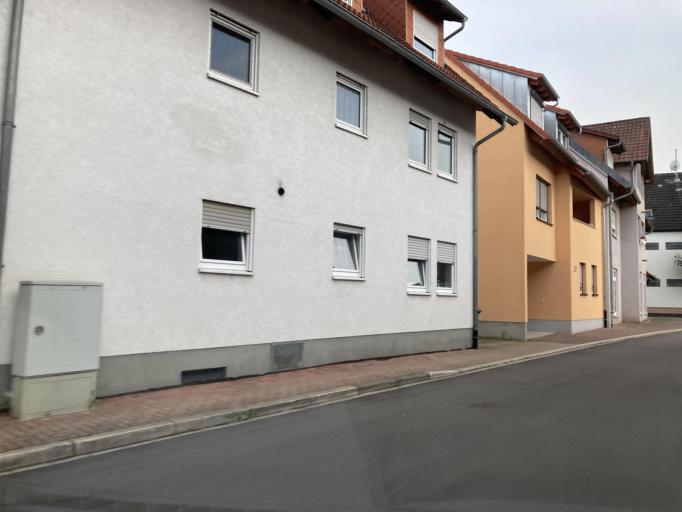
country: DE
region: Baden-Wuerttemberg
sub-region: Karlsruhe Region
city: Bretten
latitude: 49.0763
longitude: 8.7427
